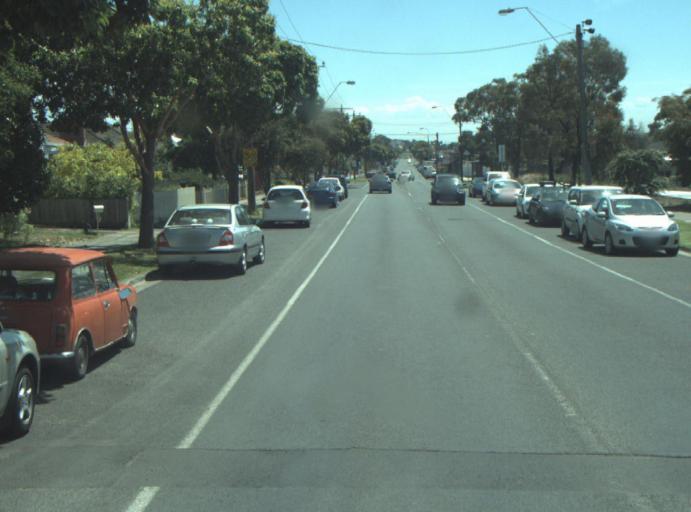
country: AU
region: Victoria
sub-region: Greater Geelong
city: Hamlyn Heights
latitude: -38.1233
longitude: 144.3278
